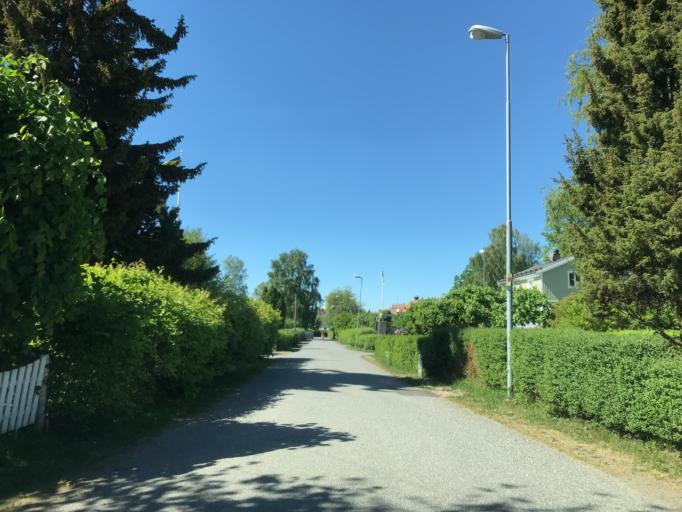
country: SE
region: Stockholm
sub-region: Sollentuna Kommun
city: Sollentuna
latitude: 59.4217
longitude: 17.9620
